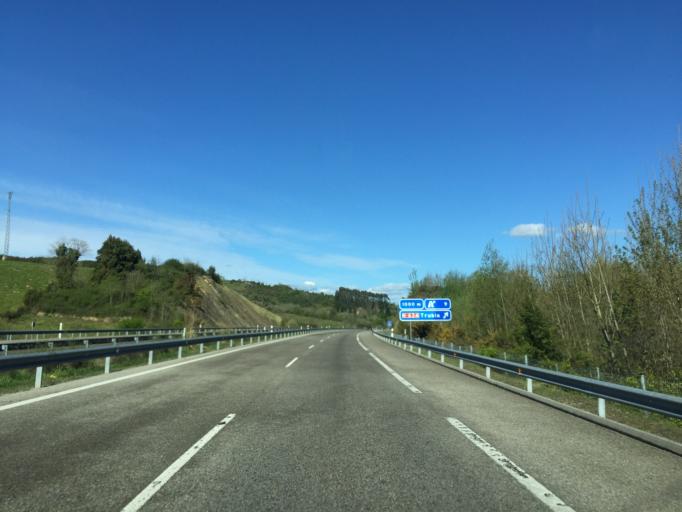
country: ES
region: Asturias
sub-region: Province of Asturias
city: Castandiello
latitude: 43.3539
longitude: -5.9344
